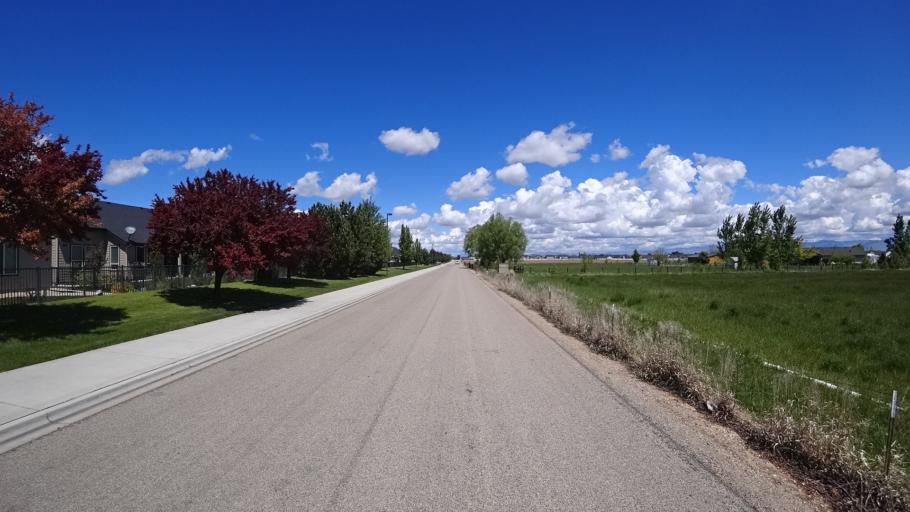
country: US
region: Idaho
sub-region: Ada County
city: Kuna
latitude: 43.5049
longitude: -116.4238
